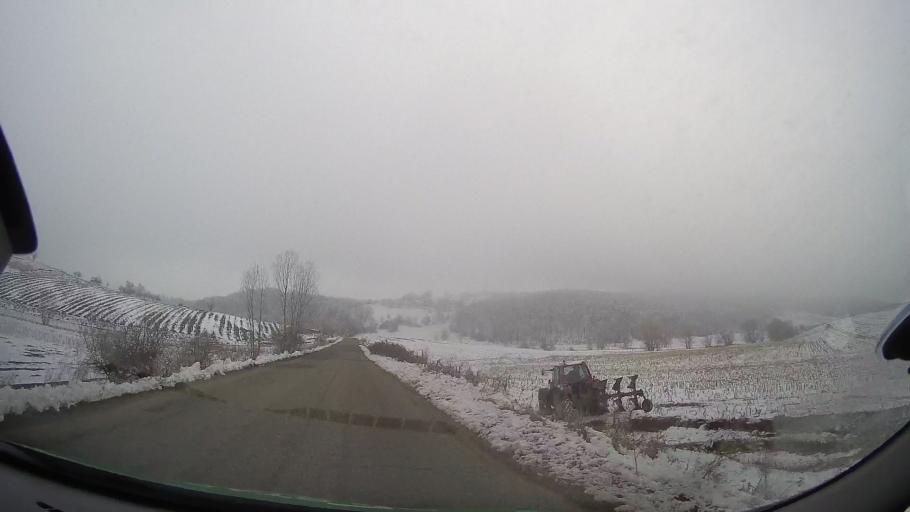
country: RO
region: Bacau
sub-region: Comuna Glavanesti
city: Frumuselu
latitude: 46.2665
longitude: 27.3158
